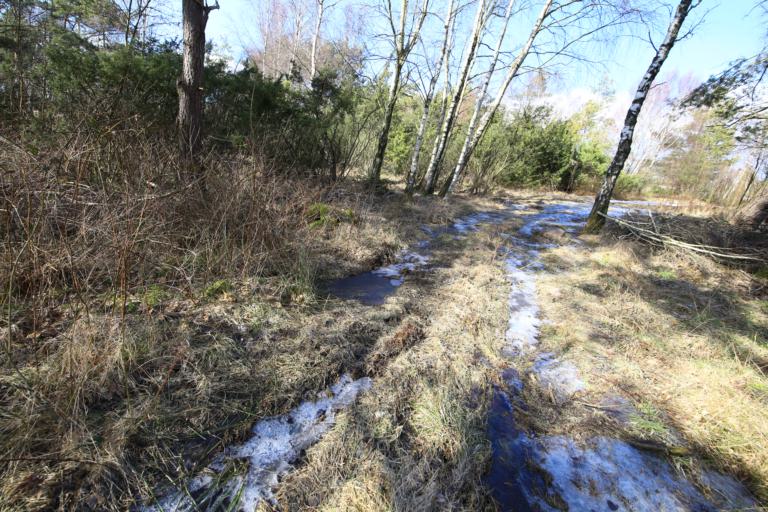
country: SE
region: Halland
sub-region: Kungsbacka Kommun
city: Frillesas
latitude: 57.2205
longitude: 12.1361
